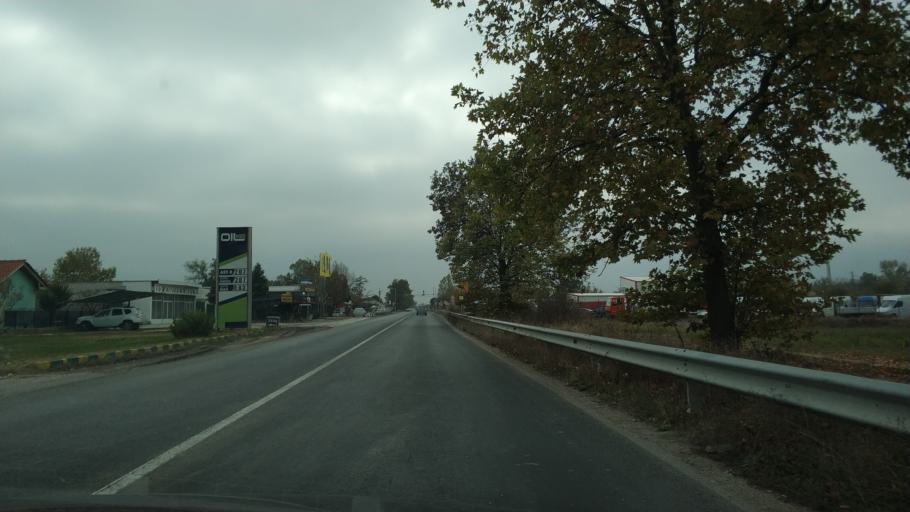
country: BG
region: Plovdiv
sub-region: Obshtina Kaloyanovo
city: Kaloyanovo
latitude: 42.2860
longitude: 24.7346
